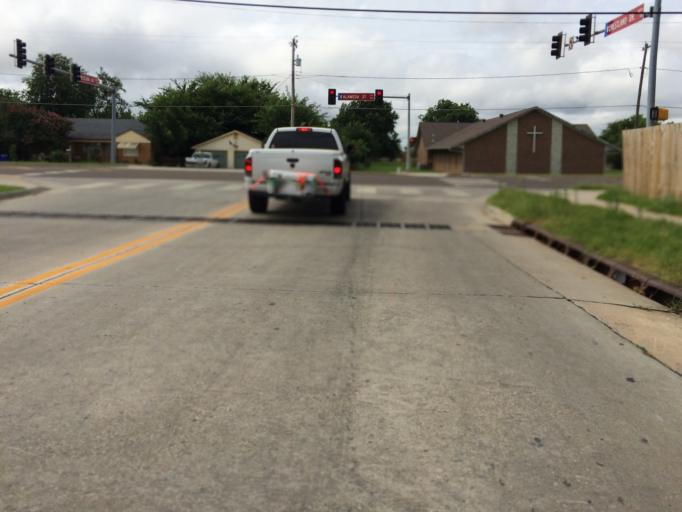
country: US
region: Oklahoma
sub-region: Cleveland County
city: Hall Park
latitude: 35.2187
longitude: -97.4134
